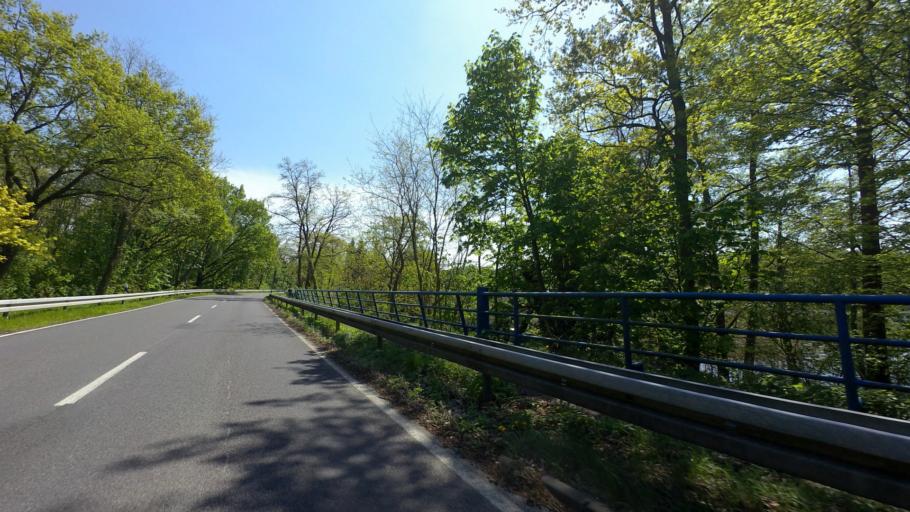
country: DE
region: Brandenburg
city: Gross Koris
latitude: 52.1853
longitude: 13.7038
